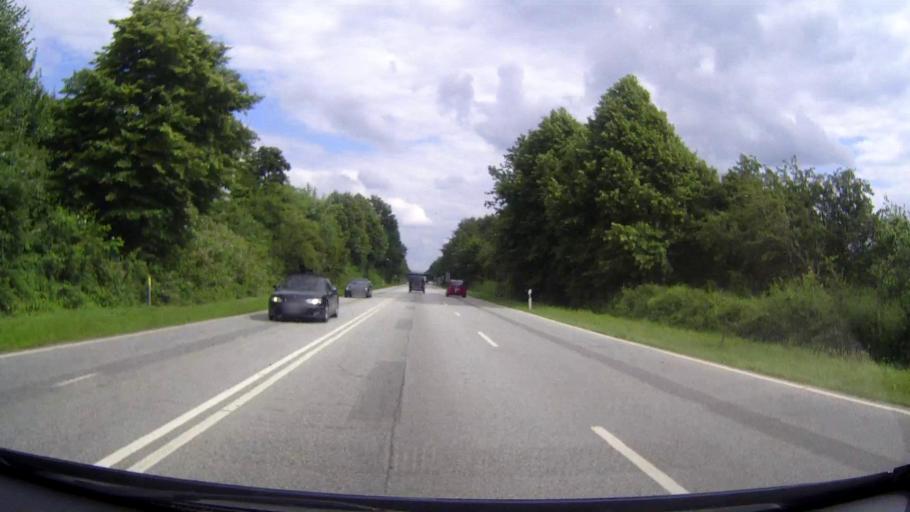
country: DE
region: Schleswig-Holstein
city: Klein Gladebrugge
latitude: 53.9305
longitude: 10.3149
